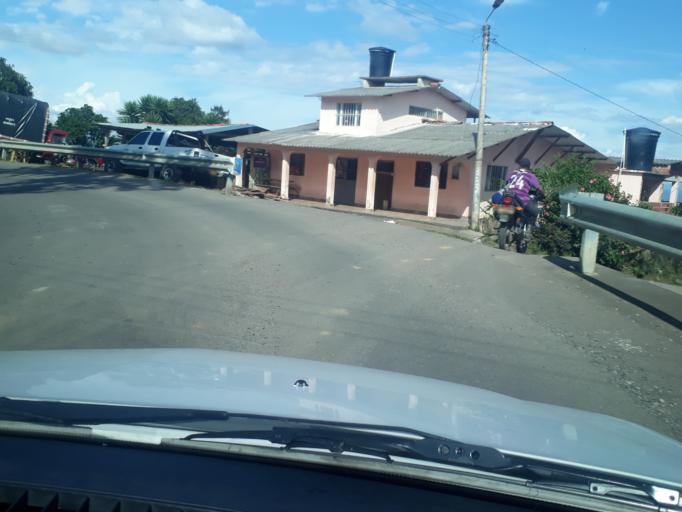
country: CO
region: Santander
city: Velez
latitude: 6.0270
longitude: -73.6547
